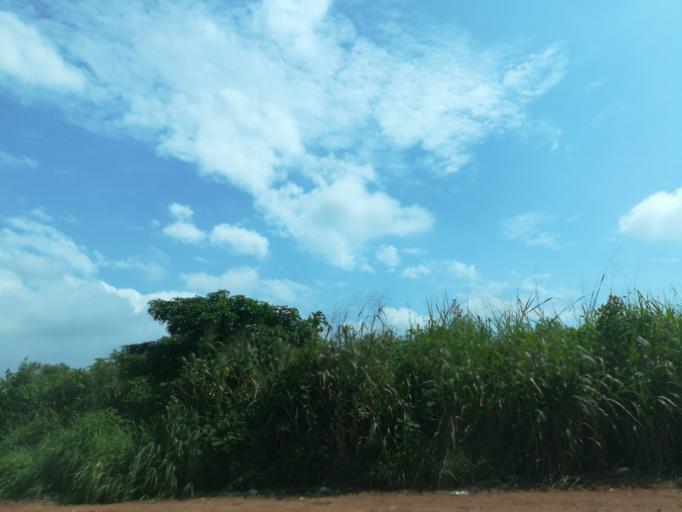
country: NG
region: Lagos
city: Ikorodu
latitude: 6.6551
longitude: 3.6923
